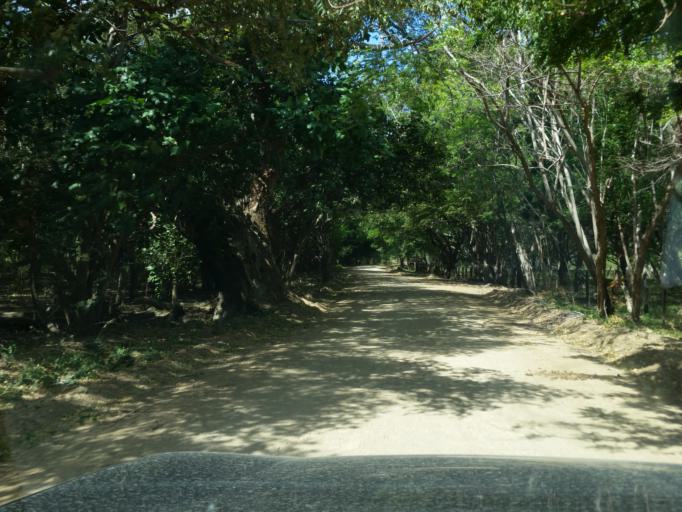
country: NI
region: Rivas
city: San Juan del Sur
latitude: 11.1418
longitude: -85.7863
